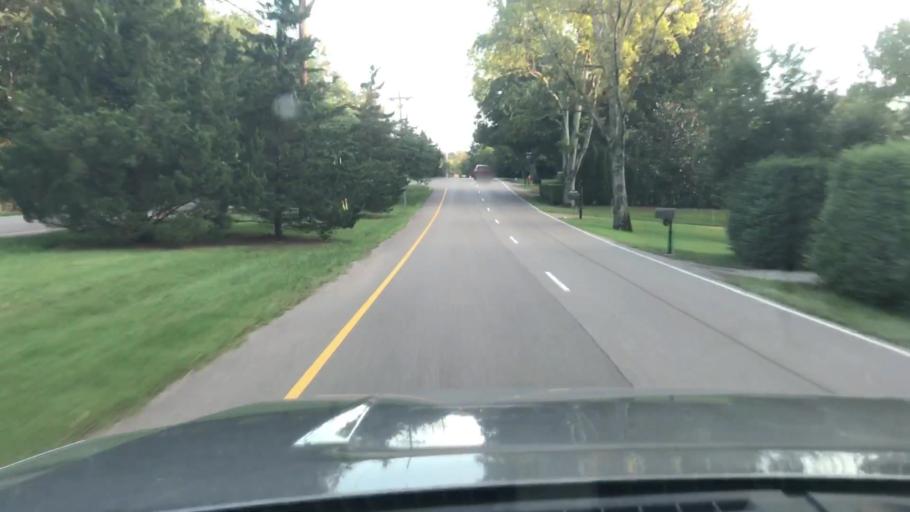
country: US
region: Tennessee
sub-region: Davidson County
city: Belle Meade
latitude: 36.0980
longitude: -86.8569
